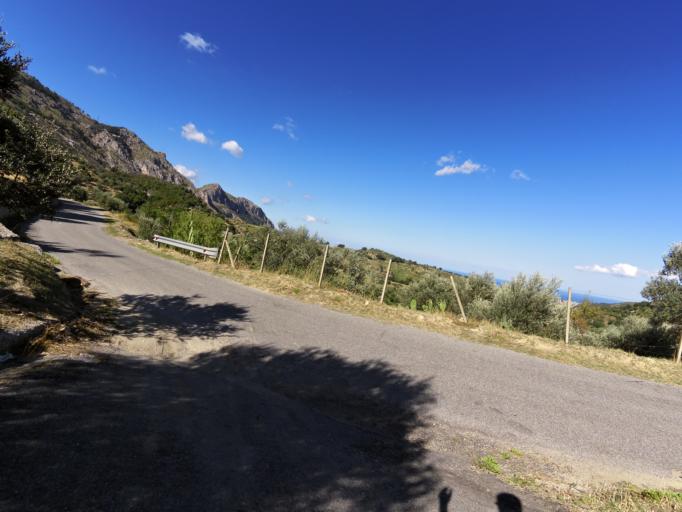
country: IT
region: Calabria
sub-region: Provincia di Reggio Calabria
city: Pazzano
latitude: 38.4543
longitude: 16.4465
